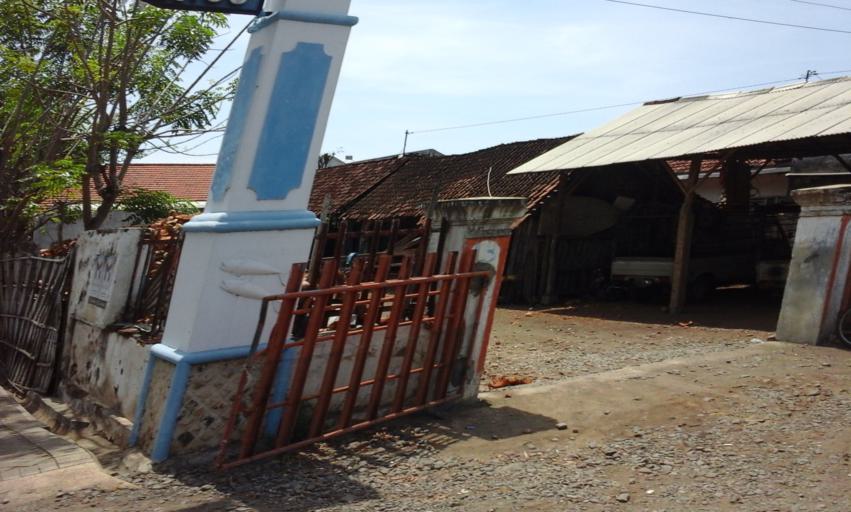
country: ID
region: East Java
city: Klatakan
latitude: -8.1562
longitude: 114.3946
